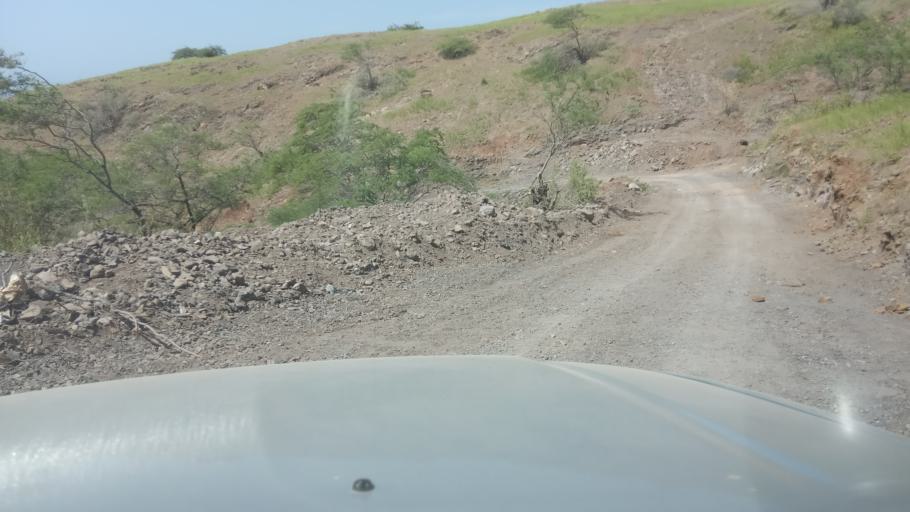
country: CV
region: Santa Catarina
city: Assomada
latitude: 15.1186
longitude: -23.7650
